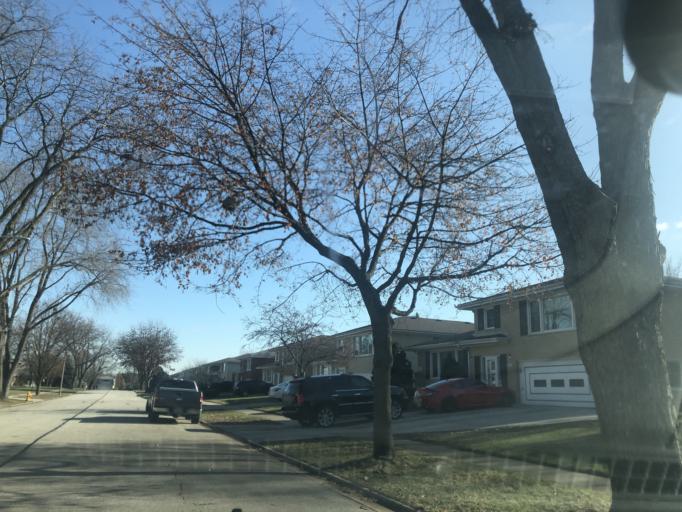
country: US
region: Illinois
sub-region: DuPage County
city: Addison
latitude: 41.9272
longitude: -88.0122
